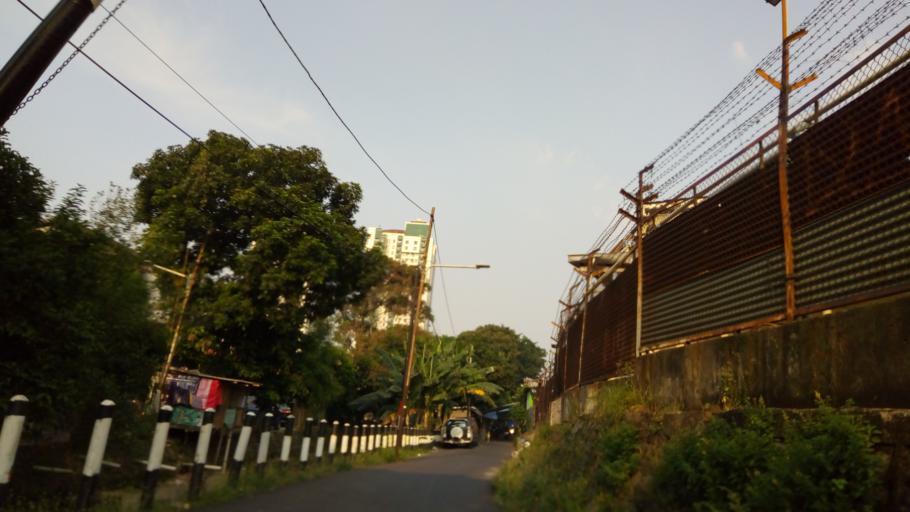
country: ID
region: Jakarta Raya
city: Jakarta
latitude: -6.1949
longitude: 106.8526
